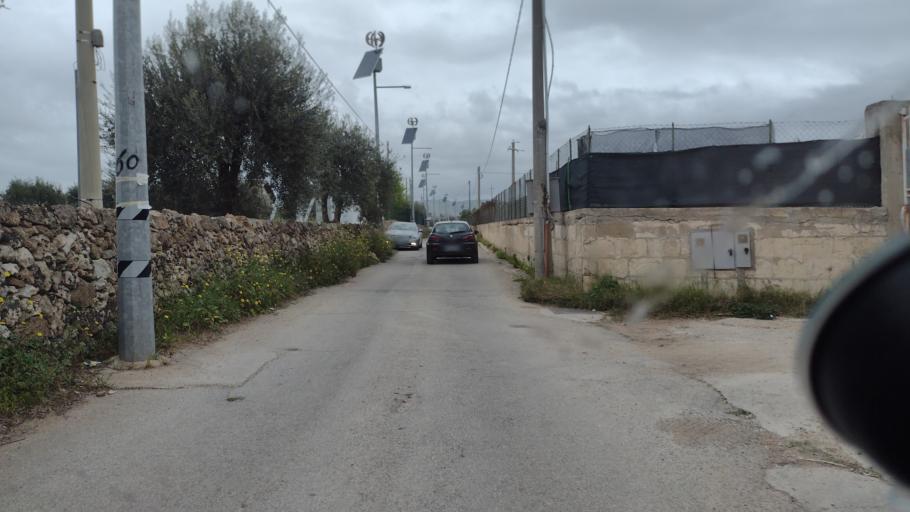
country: IT
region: Sicily
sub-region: Provincia di Siracusa
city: Avola
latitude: 36.8898
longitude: 15.1192
